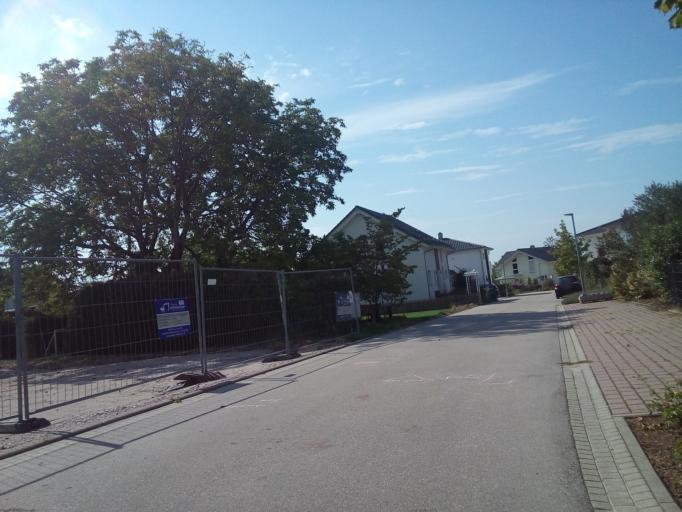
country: DE
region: Baden-Wuerttemberg
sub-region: Freiburg Region
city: Lauf
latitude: 48.6491
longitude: 8.1269
